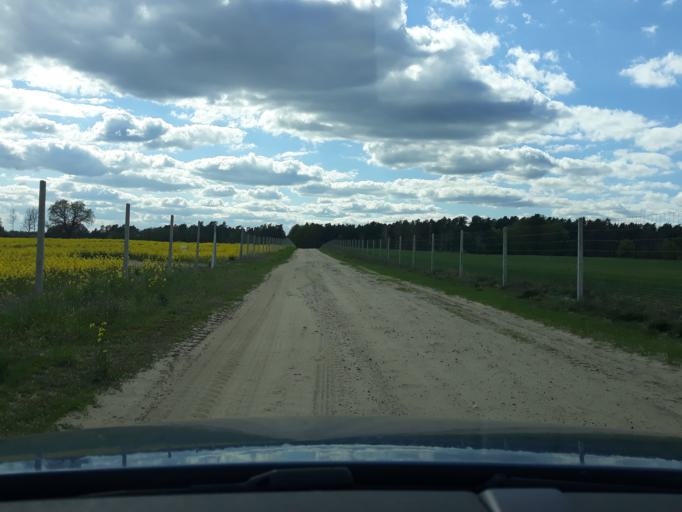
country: PL
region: Pomeranian Voivodeship
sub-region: Powiat czluchowski
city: Czluchow
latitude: 53.7194
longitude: 17.3523
